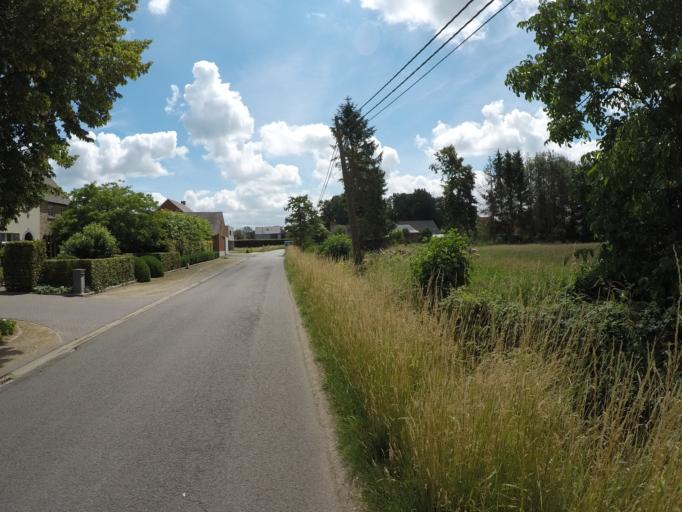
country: BE
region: Flanders
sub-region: Provincie Antwerpen
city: Vosselaar
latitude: 51.2783
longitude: 4.8811
